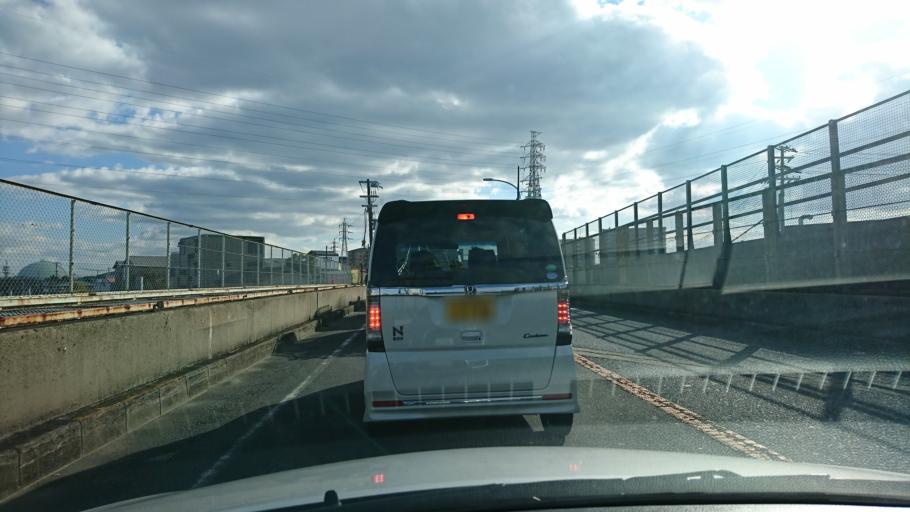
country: JP
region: Hyogo
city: Akashi
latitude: 34.6577
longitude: 134.9725
